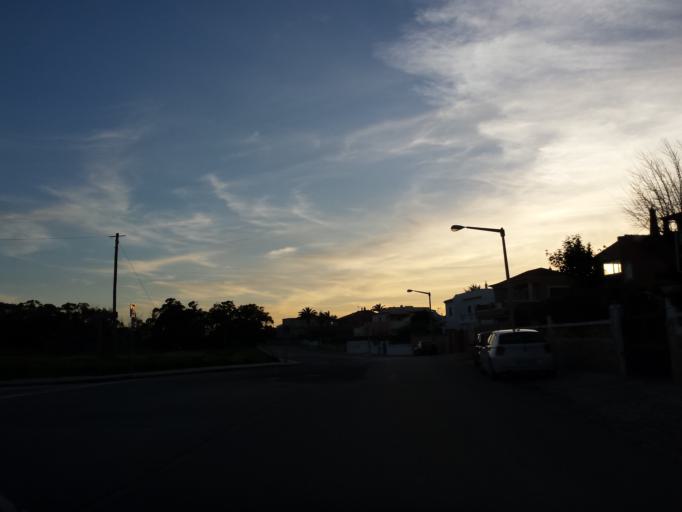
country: PT
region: Faro
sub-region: Lagos
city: Lagos
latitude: 37.0926
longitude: -8.6748
